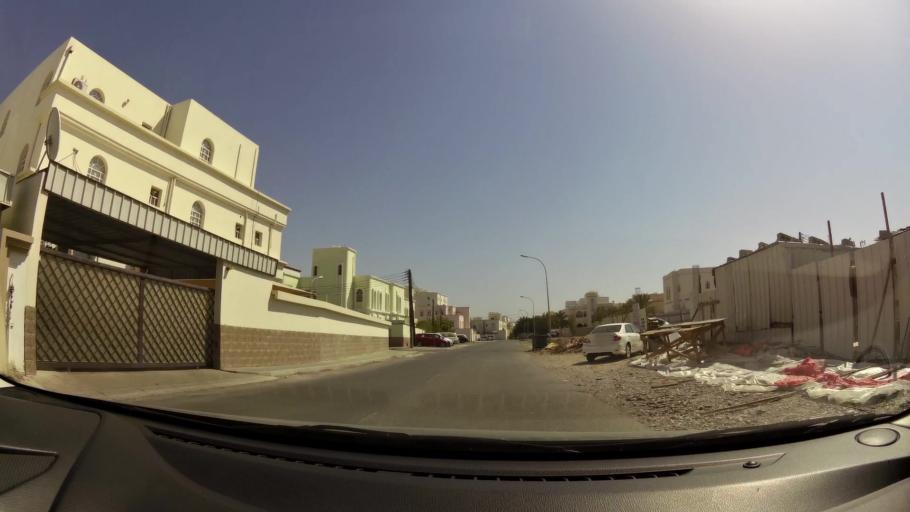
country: OM
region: Muhafazat Masqat
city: As Sib al Jadidah
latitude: 23.6344
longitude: 58.2167
